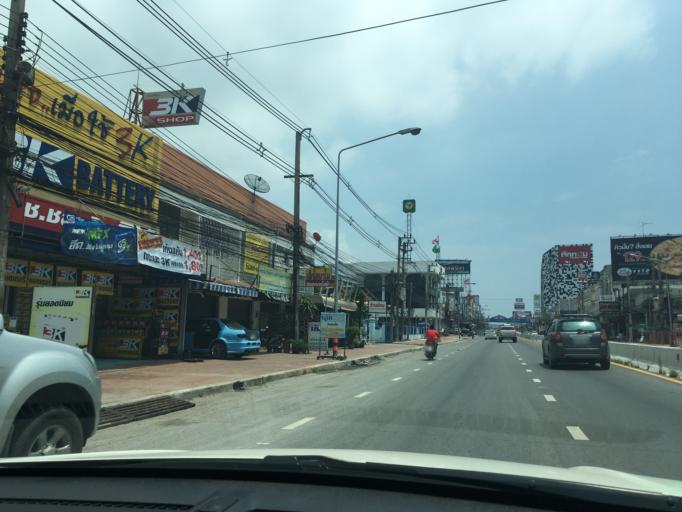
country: TH
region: Chon Buri
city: Chon Buri
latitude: 13.3438
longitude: 100.9761
